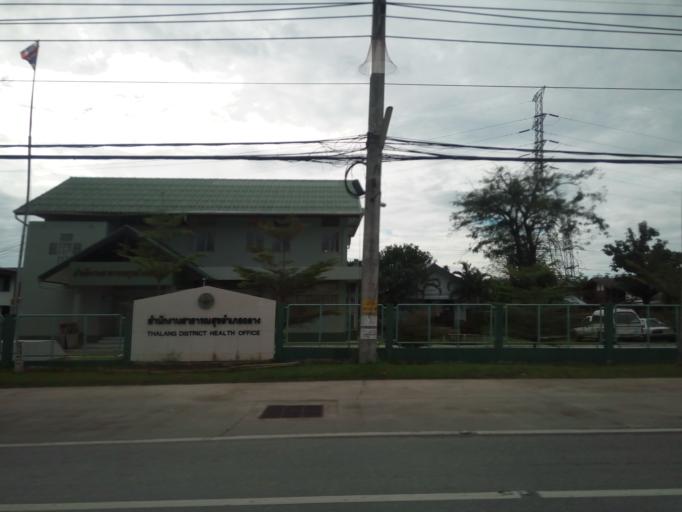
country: TH
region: Phuket
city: Thalang
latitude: 8.0344
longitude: 98.3332
